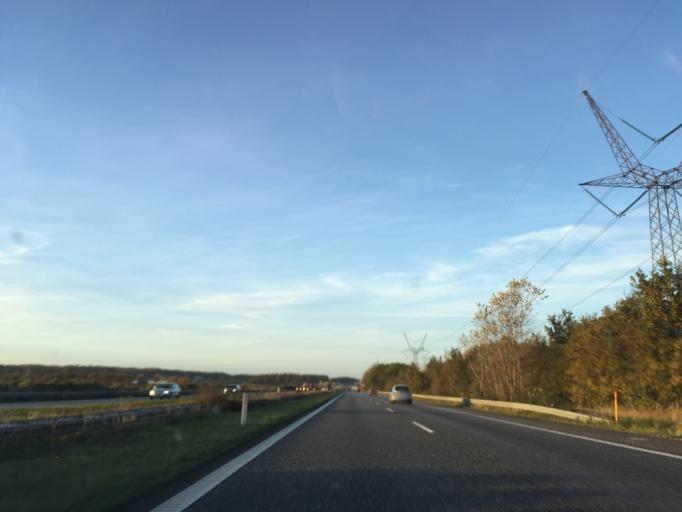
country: DK
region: South Denmark
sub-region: Kolding Kommune
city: Kolding
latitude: 55.4401
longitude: 9.4571
